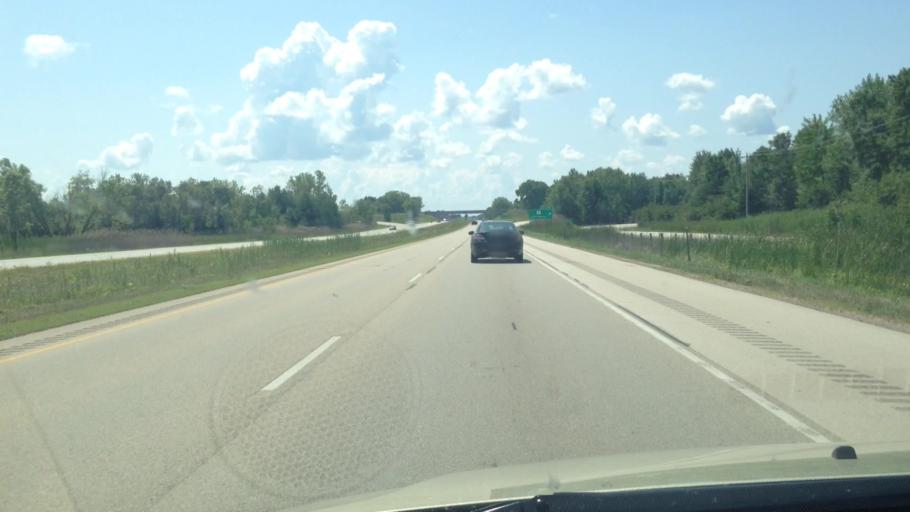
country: US
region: Wisconsin
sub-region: Brown County
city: Suamico
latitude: 44.7281
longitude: -88.0510
